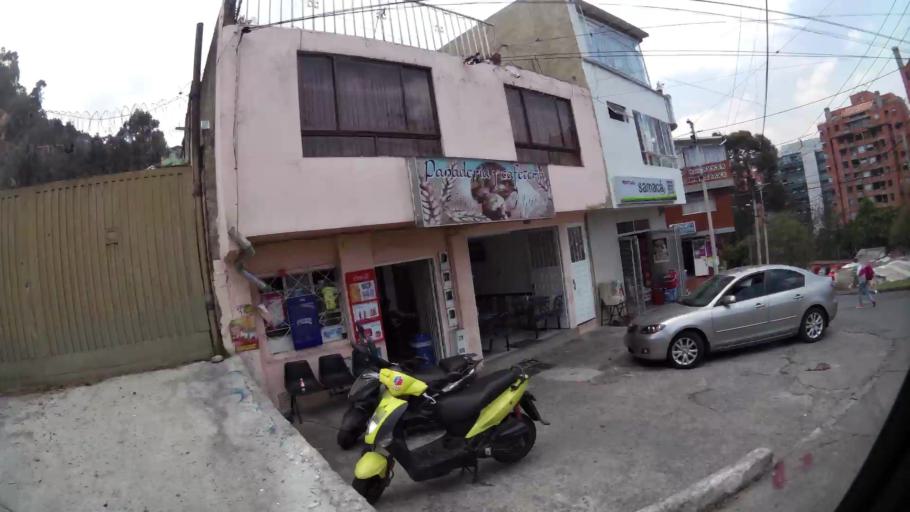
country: CO
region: Bogota D.C.
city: Barrio San Luis
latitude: 4.7037
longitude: -74.0263
